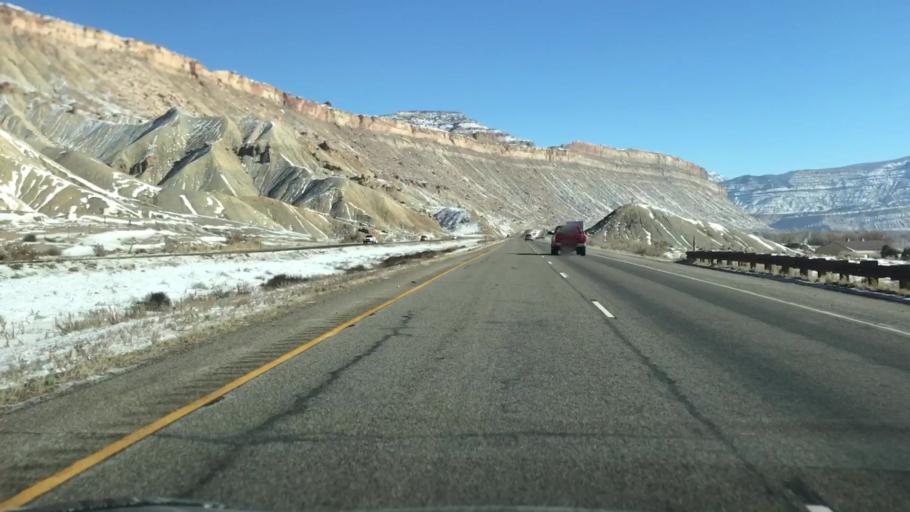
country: US
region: Colorado
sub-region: Mesa County
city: Palisade
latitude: 39.1158
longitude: -108.3962
